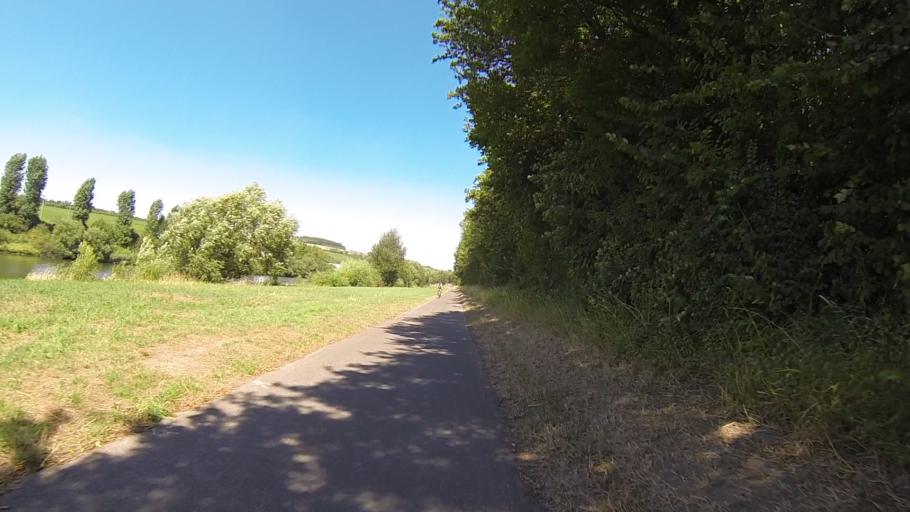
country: DE
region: Rheinland-Pfalz
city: Temmels
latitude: 49.6855
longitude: 6.4554
